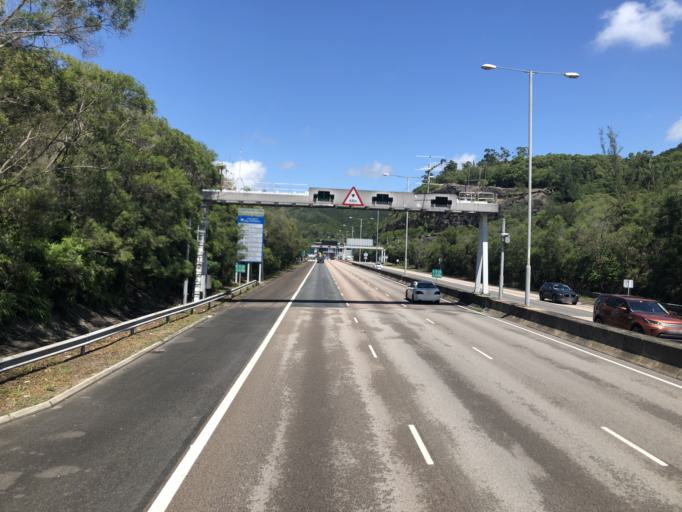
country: HK
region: Tsuen Wan
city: Tsuen Wan
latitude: 22.3714
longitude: 114.0735
